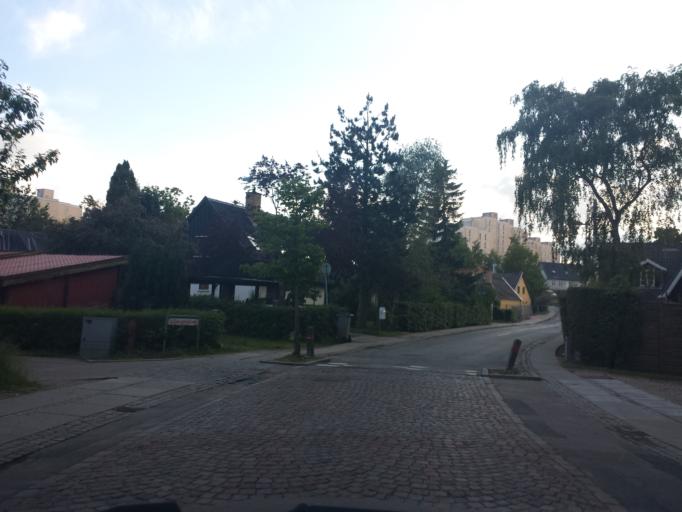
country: DK
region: Capital Region
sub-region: Ballerup Kommune
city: Malov
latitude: 55.7517
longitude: 12.3170
